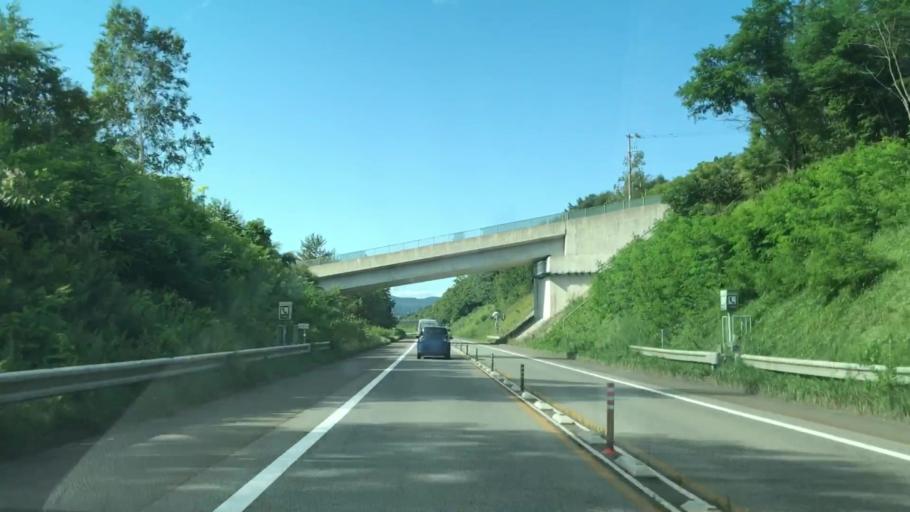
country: JP
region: Hokkaido
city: Date
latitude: 42.4724
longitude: 140.9049
